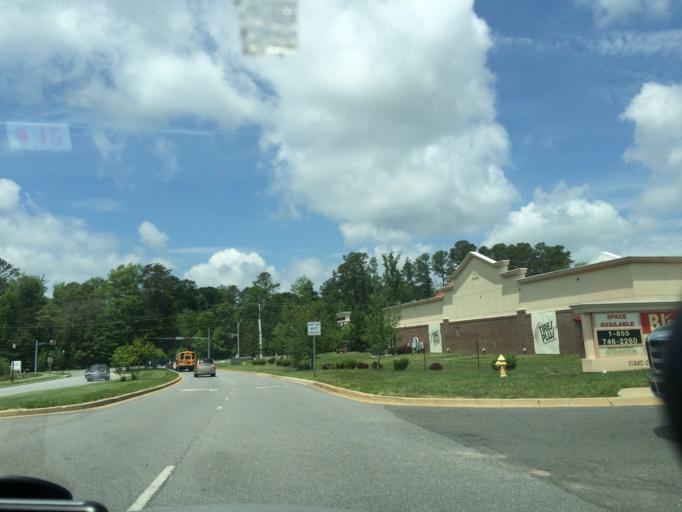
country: US
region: Maryland
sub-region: Saint Mary's County
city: California
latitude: 38.3007
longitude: -76.5217
